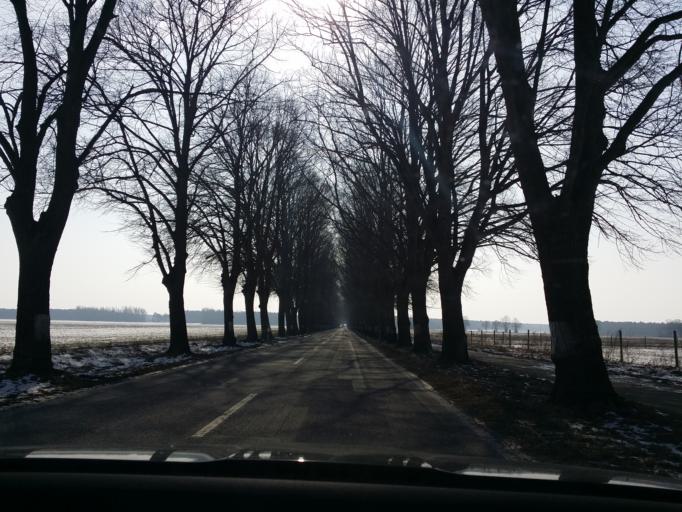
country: DE
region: Brandenburg
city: Wittstock
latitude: 53.2111
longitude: 12.5807
